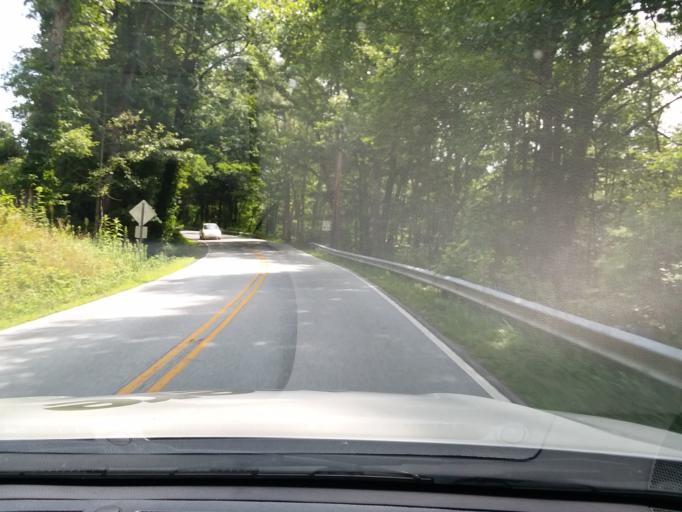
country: US
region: Georgia
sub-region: Rabun County
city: Mountain City
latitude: 35.0086
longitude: -83.3225
